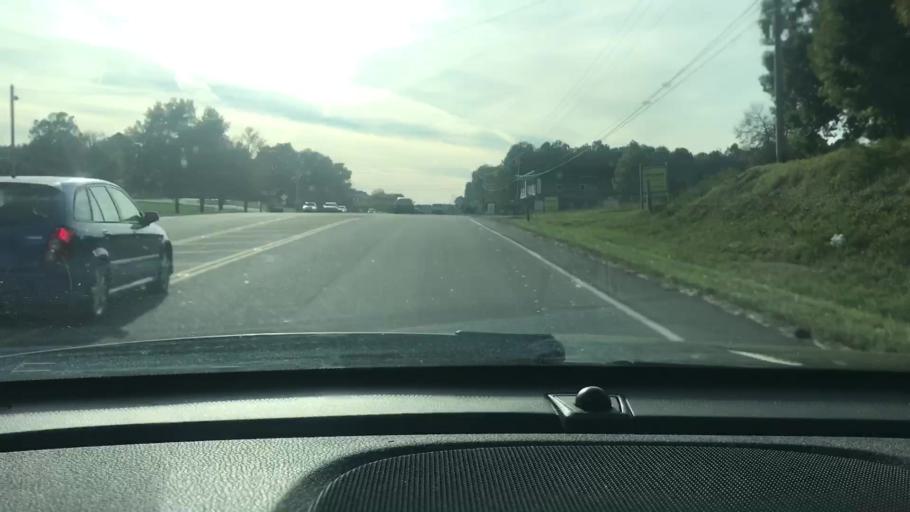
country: US
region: Tennessee
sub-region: Williamson County
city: Fairview
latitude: 35.9868
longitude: -87.1065
